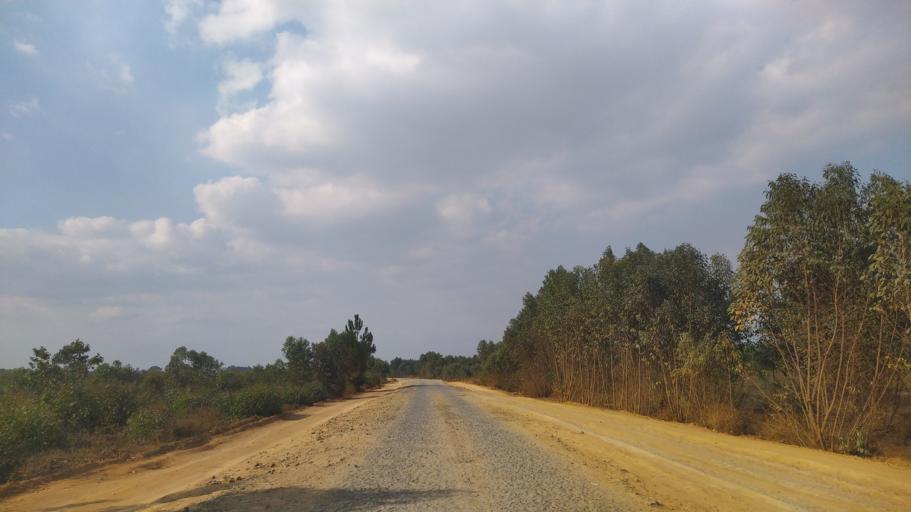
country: MG
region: Alaotra Mangoro
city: Moramanga
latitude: -18.6454
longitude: 48.2752
